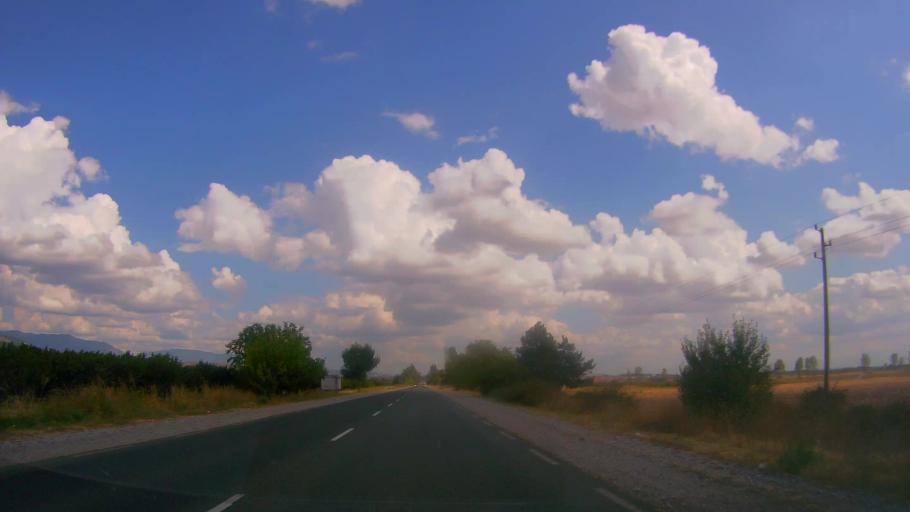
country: BG
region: Sliven
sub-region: Obshtina Sliven
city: Sliven
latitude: 42.6369
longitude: 26.2391
